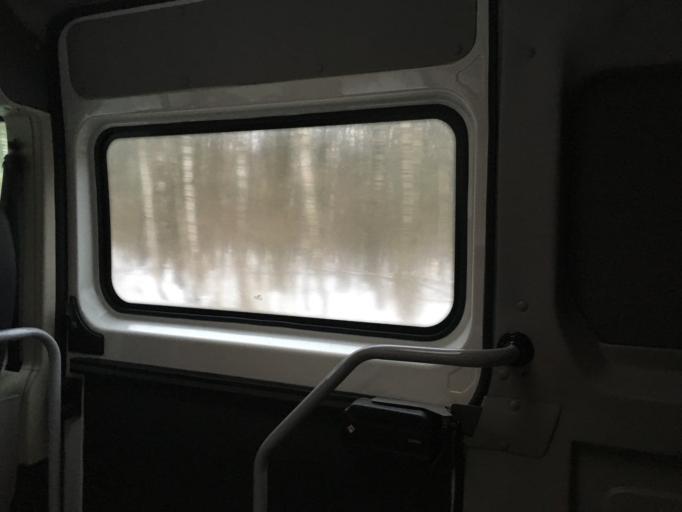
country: RU
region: Tula
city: Krapivna
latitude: 54.1278
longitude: 37.2497
